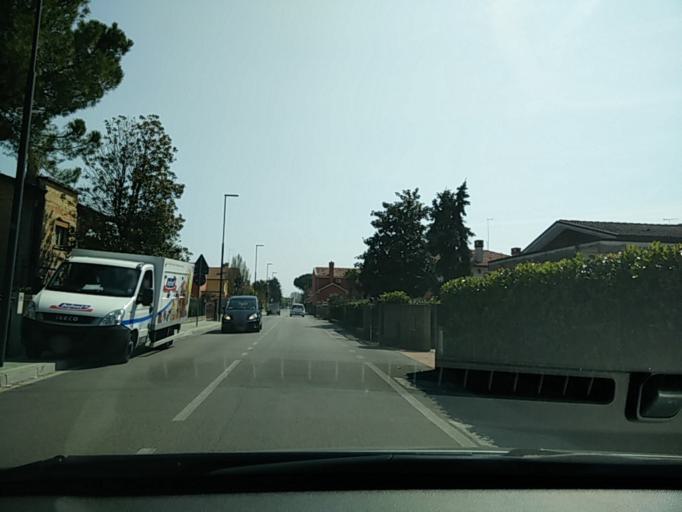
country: IT
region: Veneto
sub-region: Provincia di Venezia
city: San Dona di Piave
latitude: 45.6211
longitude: 12.5666
